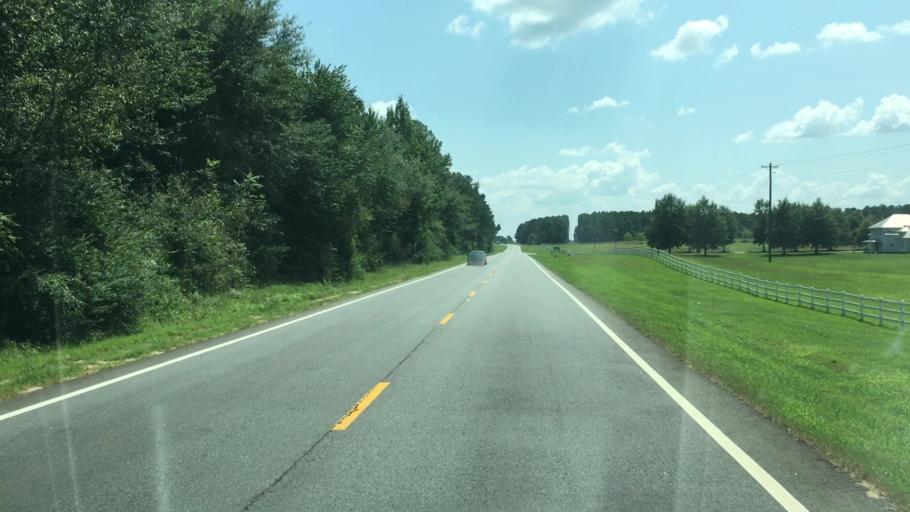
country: US
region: Georgia
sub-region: Oconee County
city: Watkinsville
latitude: 33.7611
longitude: -83.4343
